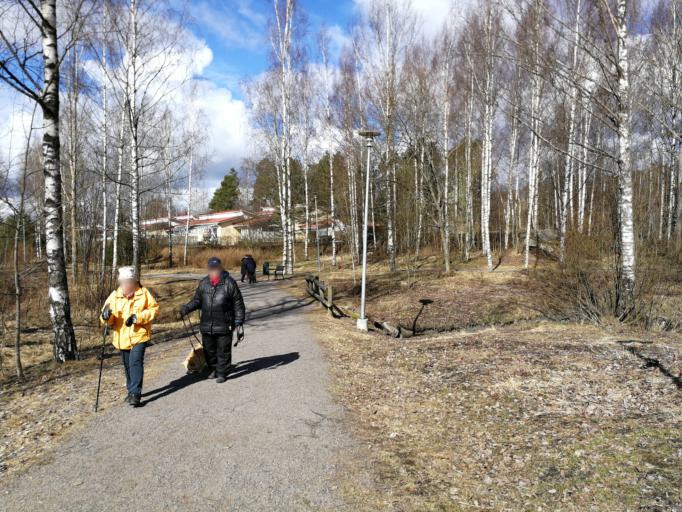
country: FI
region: Uusimaa
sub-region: Helsinki
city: Koukkuniemi
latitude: 60.1612
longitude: 24.7329
